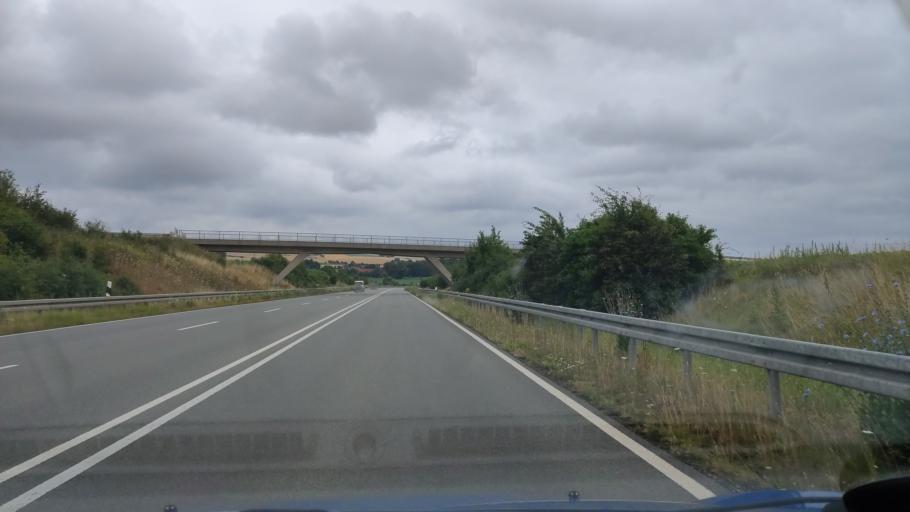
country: DE
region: Lower Saxony
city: Bad Munder am Deister
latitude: 52.2243
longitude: 9.4268
